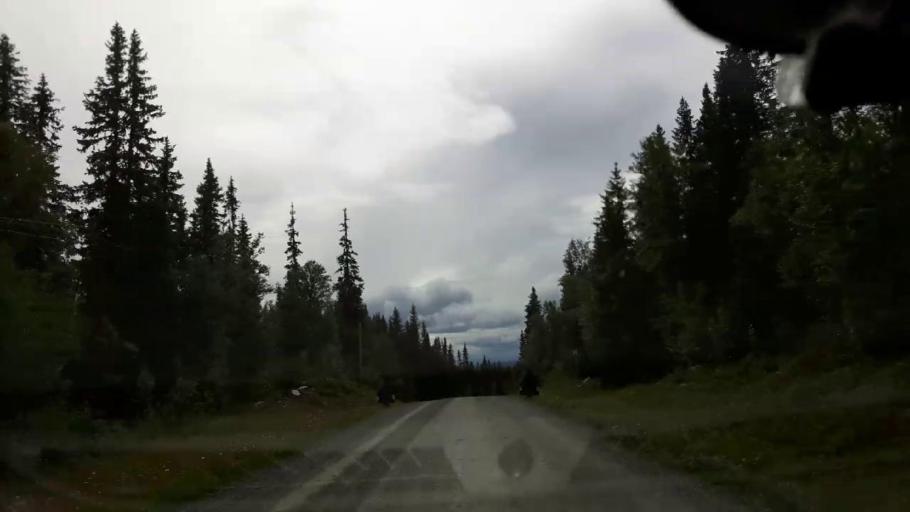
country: SE
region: Jaemtland
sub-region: Krokoms Kommun
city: Valla
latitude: 63.7360
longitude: 13.8372
